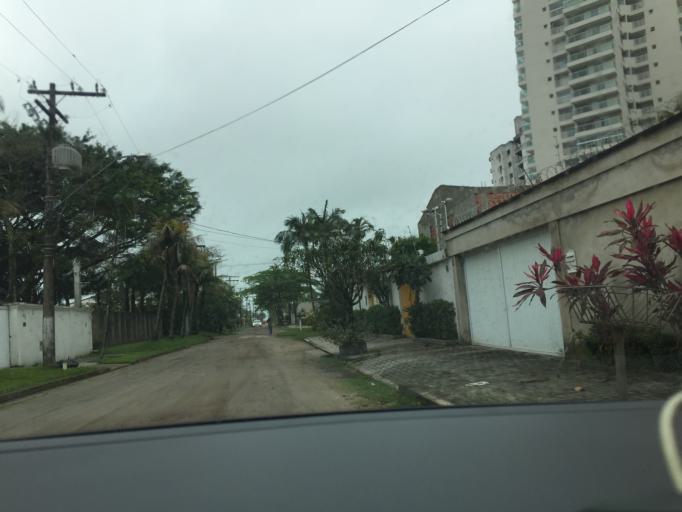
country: BR
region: Sao Paulo
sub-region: Guaruja
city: Guaruja
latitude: -23.9805
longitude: -46.2200
